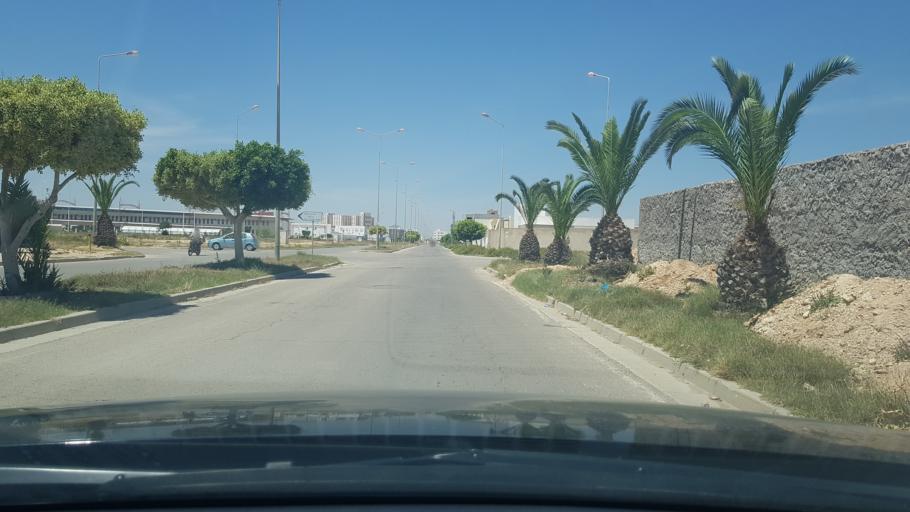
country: TN
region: Safaqis
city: Al Qarmadah
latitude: 34.8363
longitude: 10.7608
